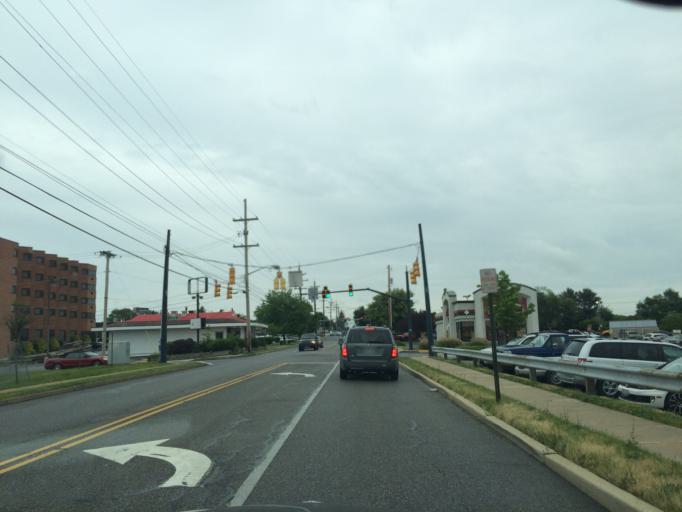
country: US
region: Maryland
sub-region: Washington County
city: Hagerstown
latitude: 39.6359
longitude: -77.7106
